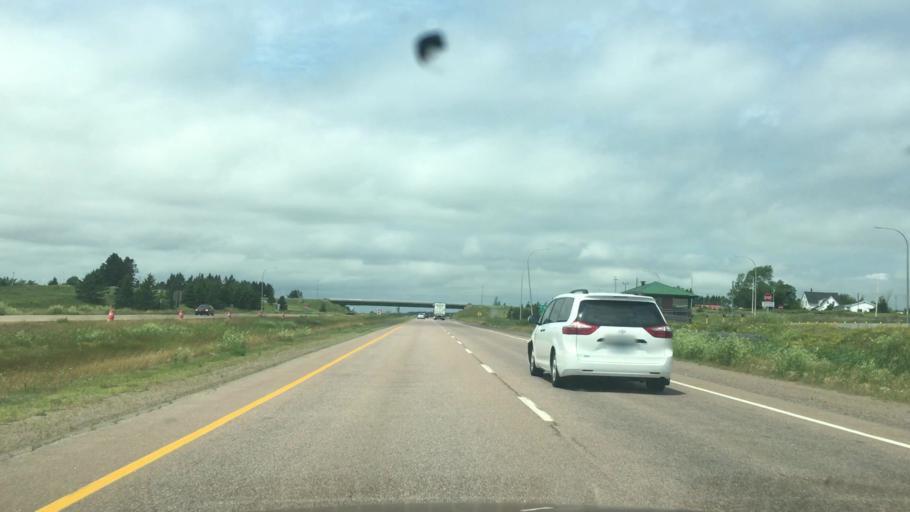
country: CA
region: Nova Scotia
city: Amherst
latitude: 45.8510
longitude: -64.2508
